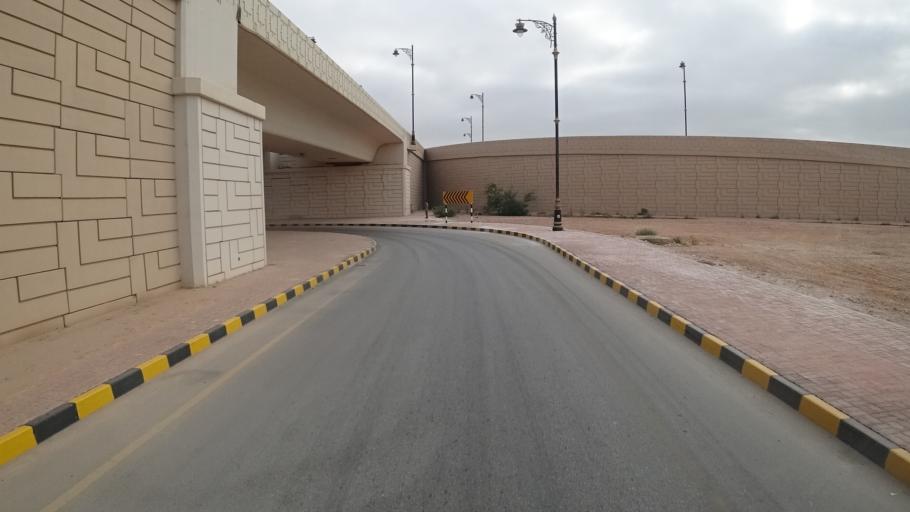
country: OM
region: Zufar
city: Salalah
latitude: 17.0159
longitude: 54.0564
